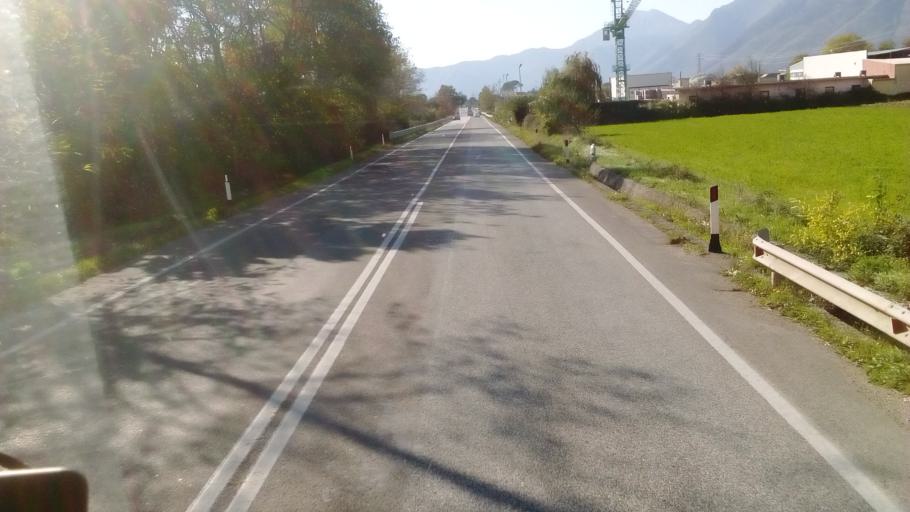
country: IT
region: Molise
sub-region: Provincia di Isernia
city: Taverna Ravindola
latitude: 41.5063
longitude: 14.1076
